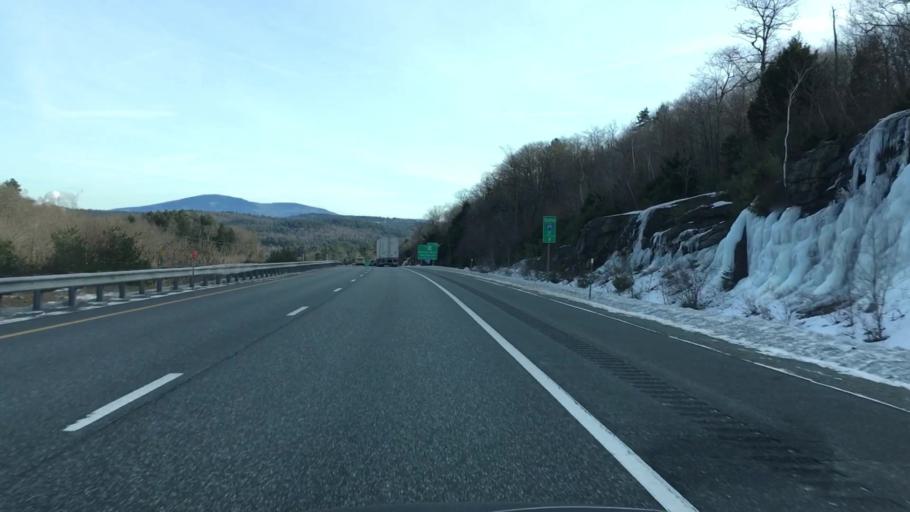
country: US
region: New Hampshire
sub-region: Sullivan County
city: Sunapee
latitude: 43.4457
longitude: -72.0790
